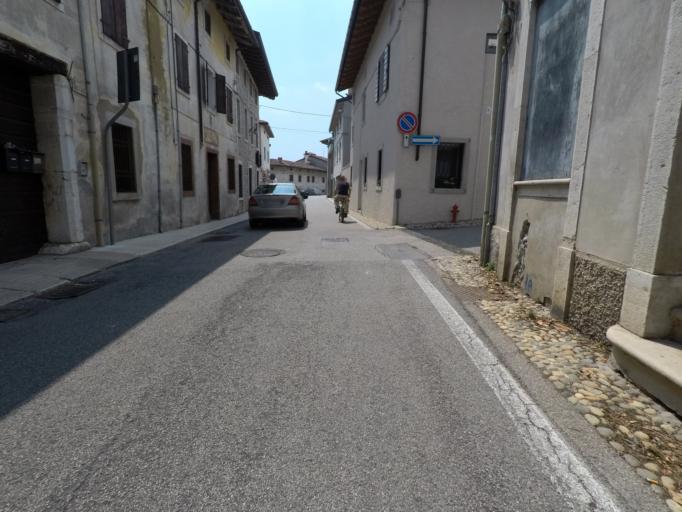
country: IT
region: Friuli Venezia Giulia
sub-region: Provincia di Pordenone
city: Aviano-Castello
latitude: 46.0663
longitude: 12.5872
